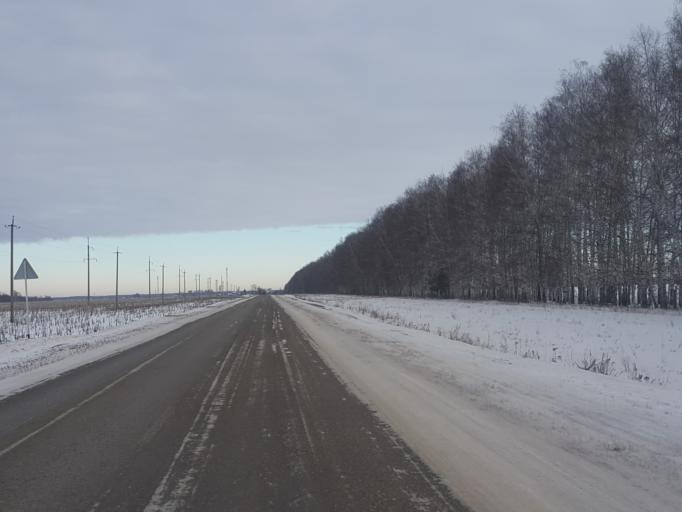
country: RU
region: Tambov
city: Rasskazovo
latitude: 52.8124
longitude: 41.7918
